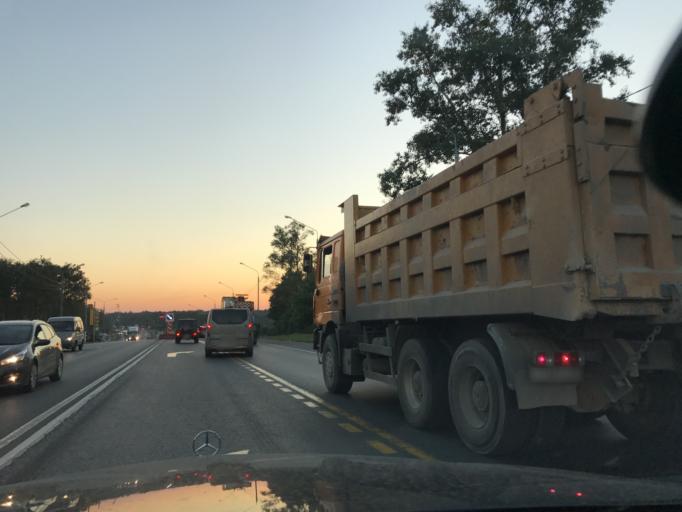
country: RU
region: Vladimir
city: Pokrov
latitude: 55.8999
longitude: 39.0650
